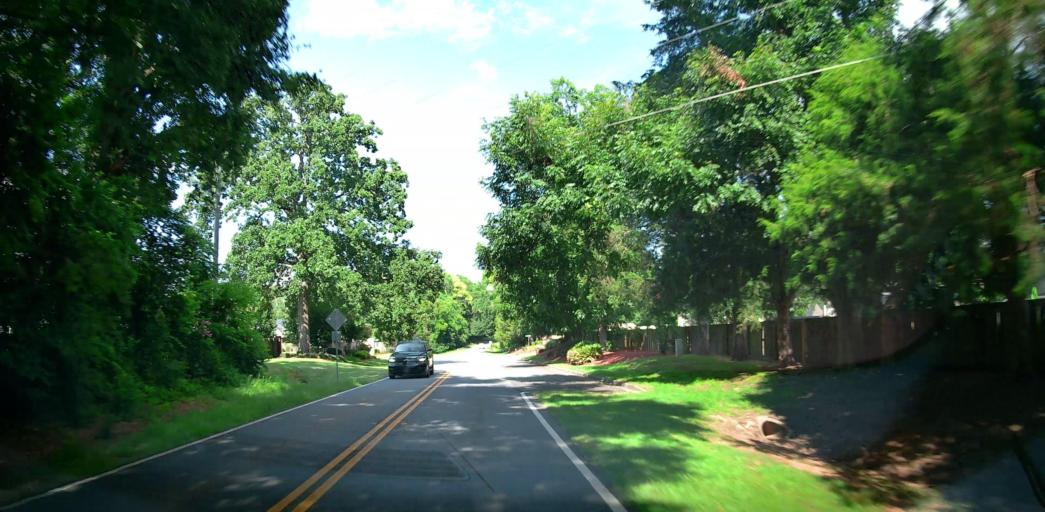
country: US
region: Georgia
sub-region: Houston County
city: Perry
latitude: 32.5343
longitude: -83.6708
